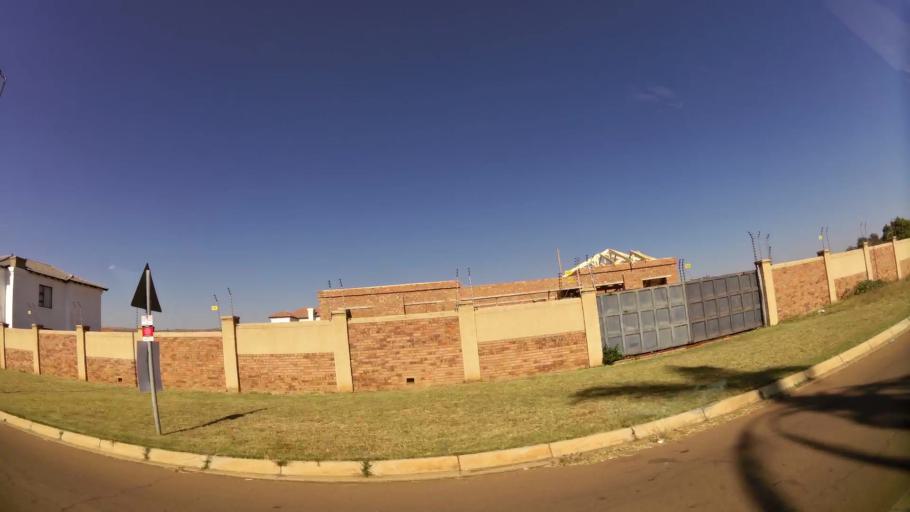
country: ZA
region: North-West
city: Ga-Rankuwa
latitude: -25.6510
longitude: 28.0817
